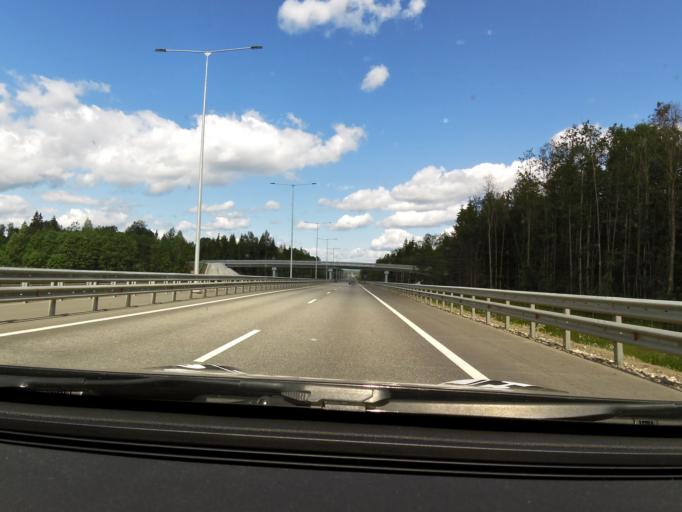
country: RU
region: Tverskaya
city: Vydropuzhsk
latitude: 57.2948
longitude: 34.7780
